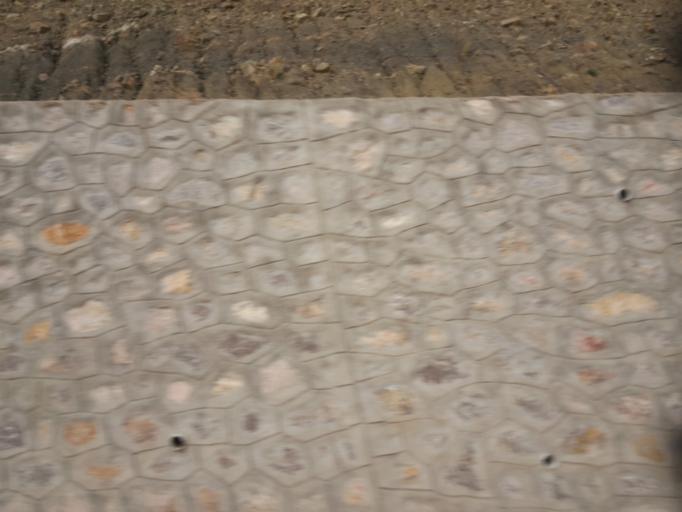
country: TR
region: Sinop
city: Duragan
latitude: 41.4657
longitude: 35.0435
